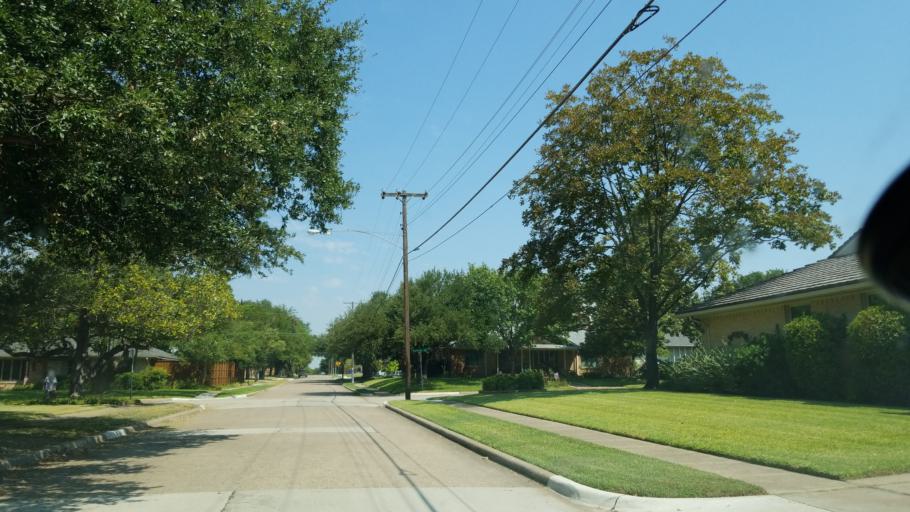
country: US
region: Texas
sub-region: Dallas County
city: Richardson
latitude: 32.8730
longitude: -96.7127
